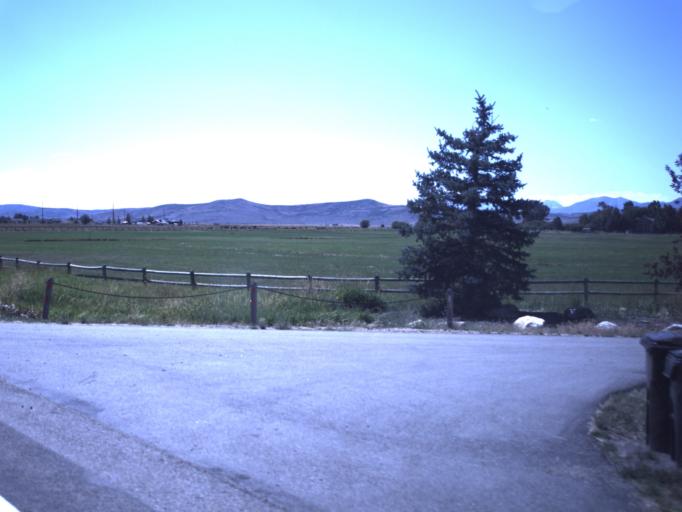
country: US
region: Utah
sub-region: Summit County
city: Kamas
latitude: 40.6628
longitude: -111.2808
